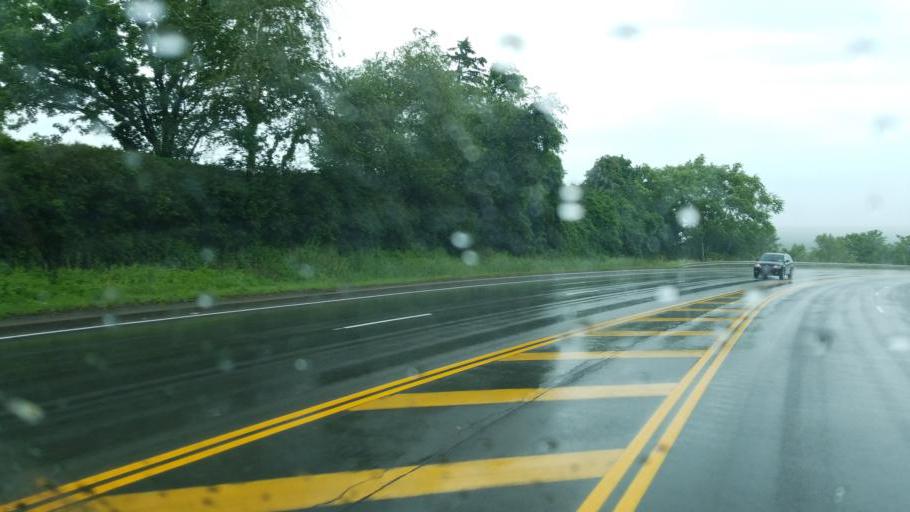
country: US
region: New York
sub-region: Niagara County
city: Lewiston
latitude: 43.1626
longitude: -79.0379
